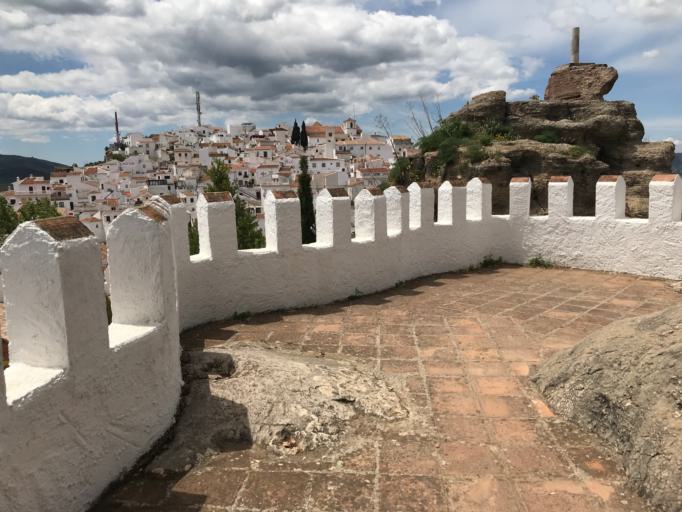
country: ES
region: Andalusia
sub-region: Provincia de Malaga
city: Comares
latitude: 36.8498
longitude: -4.2462
